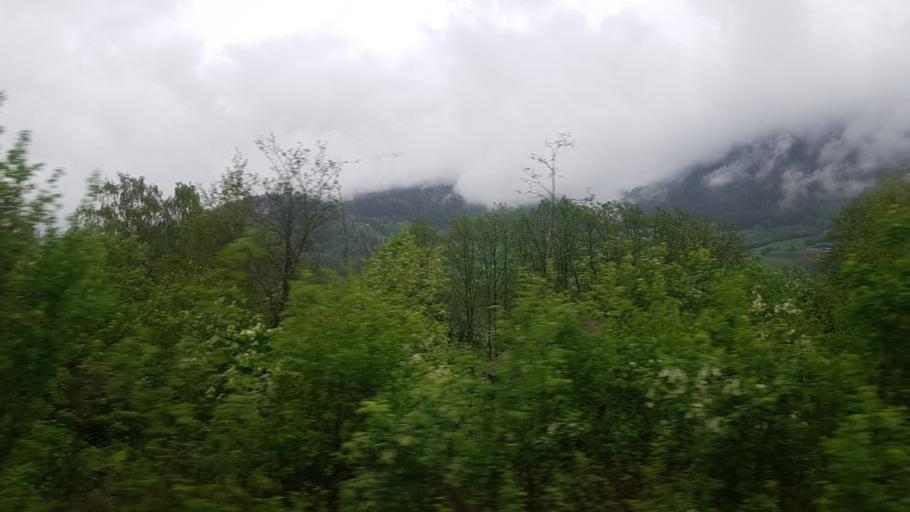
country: NO
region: Oppland
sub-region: Oyer
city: Tretten
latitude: 61.4020
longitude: 10.2427
